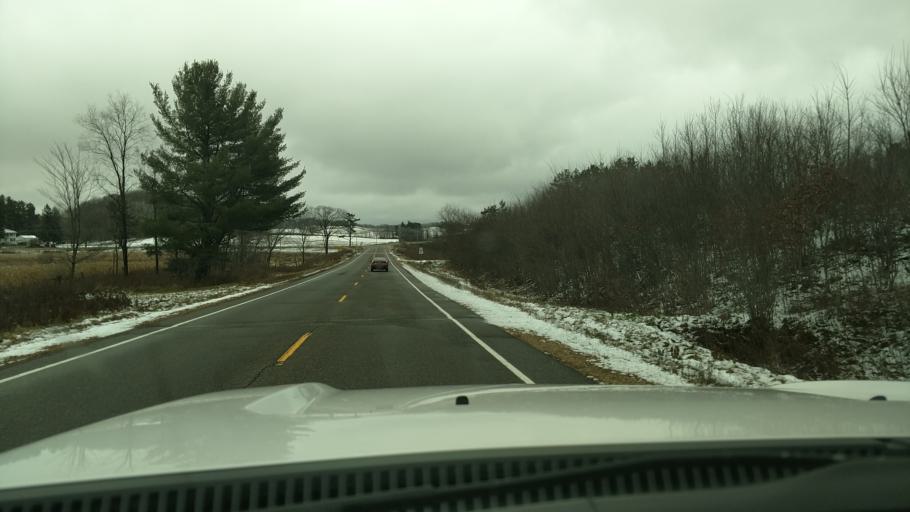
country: US
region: Wisconsin
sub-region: Dunn County
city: Boyceville
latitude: 45.1400
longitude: -91.9753
